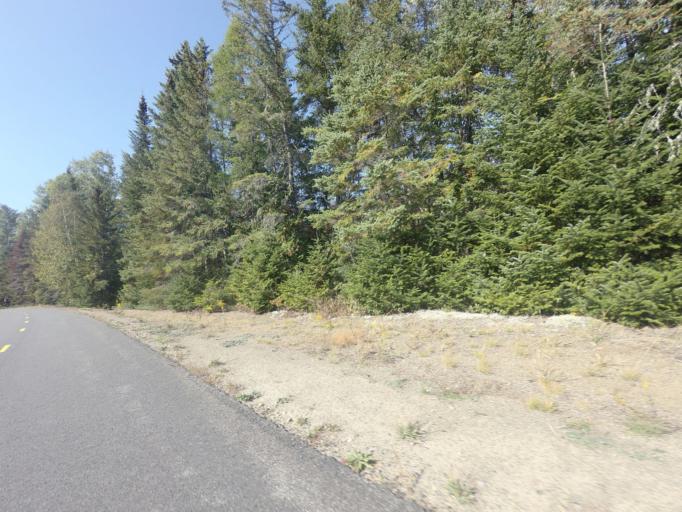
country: CA
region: Quebec
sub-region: Laurentides
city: Mont-Tremblant
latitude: 46.1263
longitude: -74.5312
